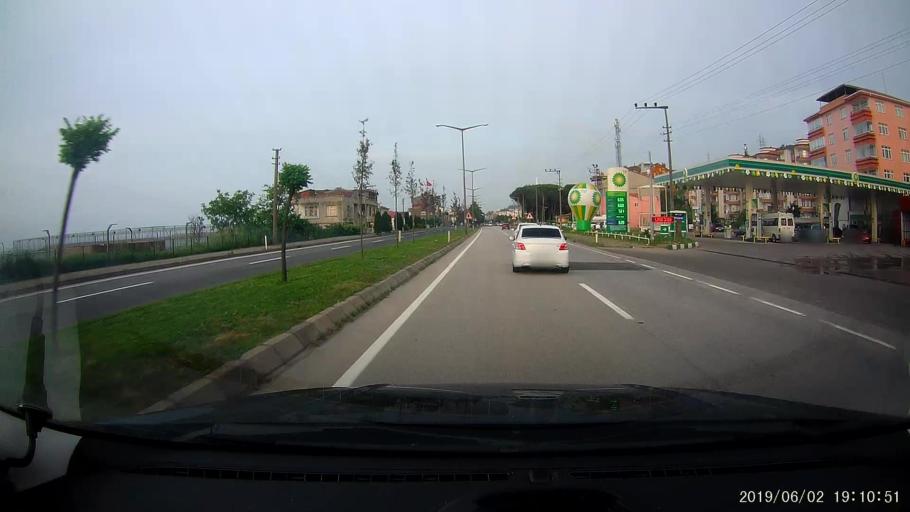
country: TR
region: Ordu
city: Gulyali
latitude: 40.9676
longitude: 38.0524
